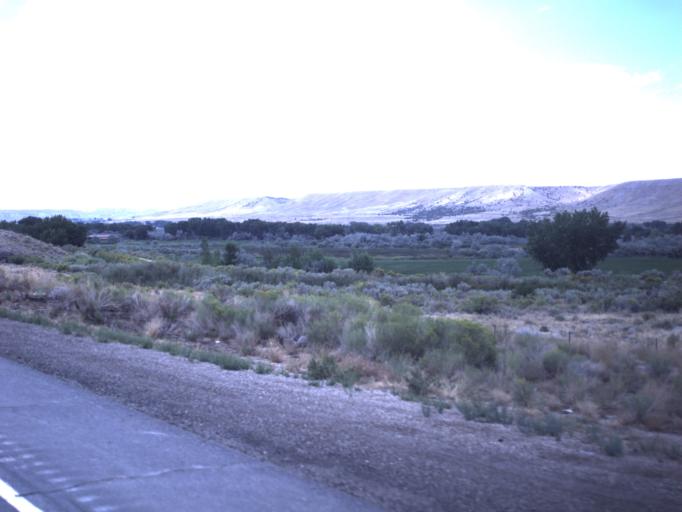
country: US
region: Utah
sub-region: Duchesne County
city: Duchesne
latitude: 40.1544
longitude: -110.2453
